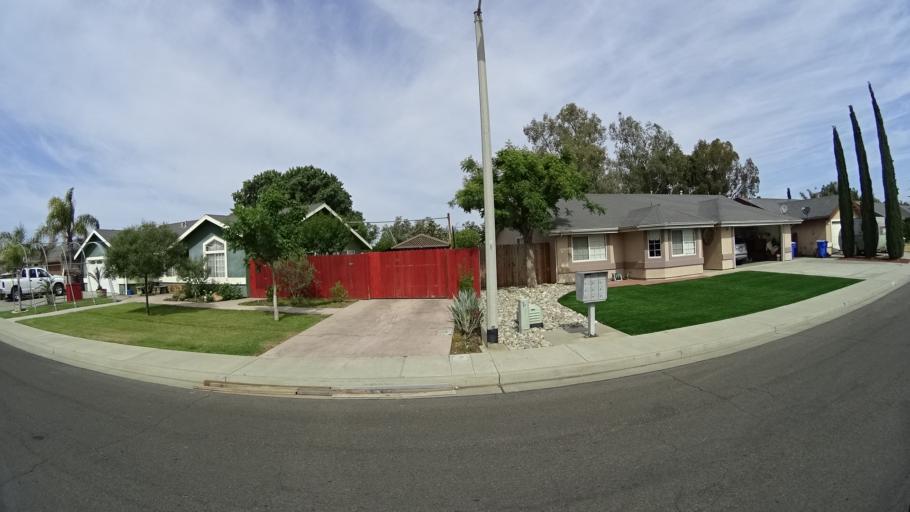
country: US
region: California
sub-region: Kings County
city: Hanford
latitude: 36.3113
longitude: -119.6652
